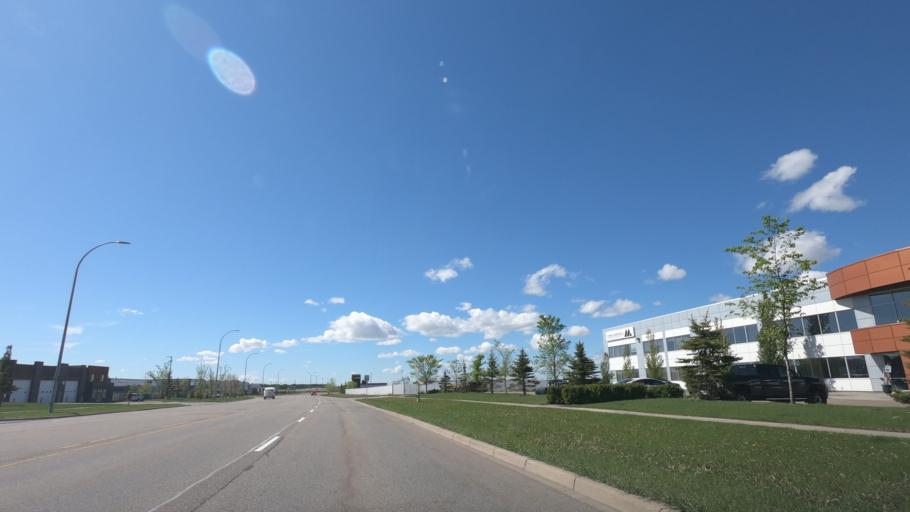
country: CA
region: Alberta
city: Airdrie
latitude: 51.2604
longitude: -113.9954
